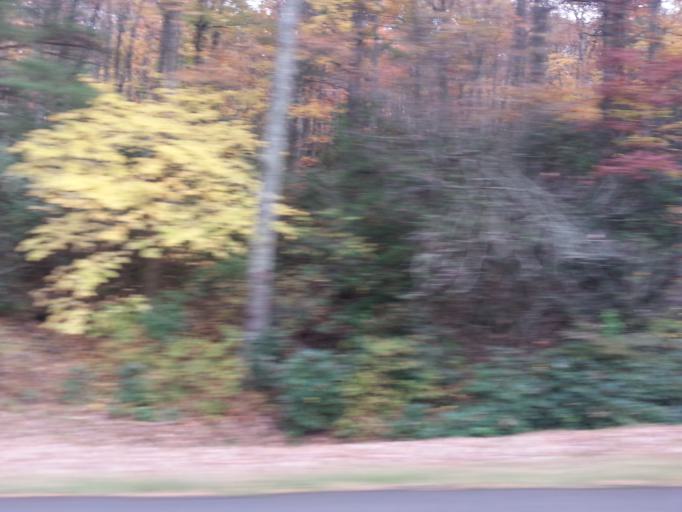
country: US
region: North Carolina
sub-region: Ashe County
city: Jefferson
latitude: 36.3069
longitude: -81.3623
